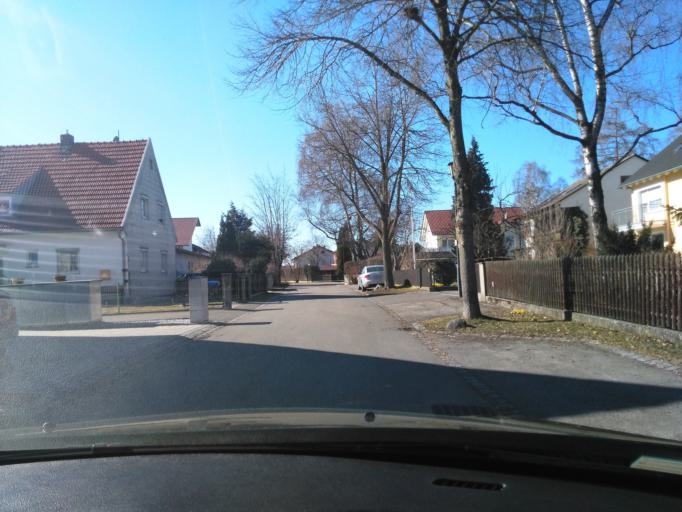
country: DE
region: Bavaria
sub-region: Upper Bavaria
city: Mammendorf
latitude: 48.2090
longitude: 11.1729
